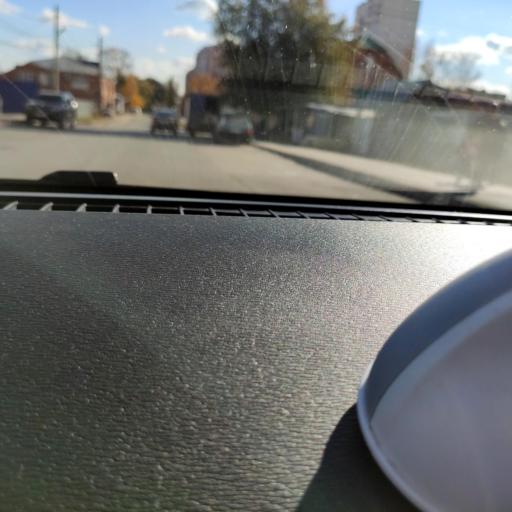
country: RU
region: Samara
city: Samara
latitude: 53.1892
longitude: 50.2146
